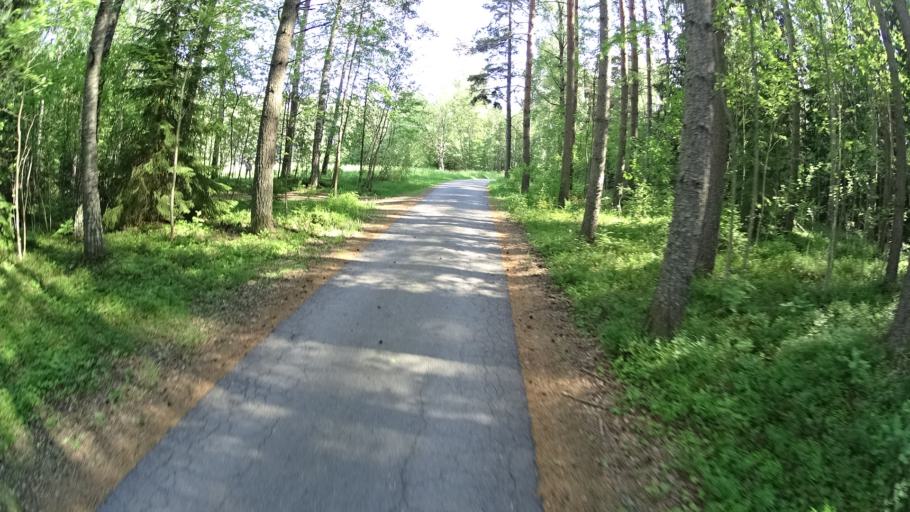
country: FI
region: Uusimaa
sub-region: Helsinki
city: Vantaa
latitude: 60.2354
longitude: 25.1829
